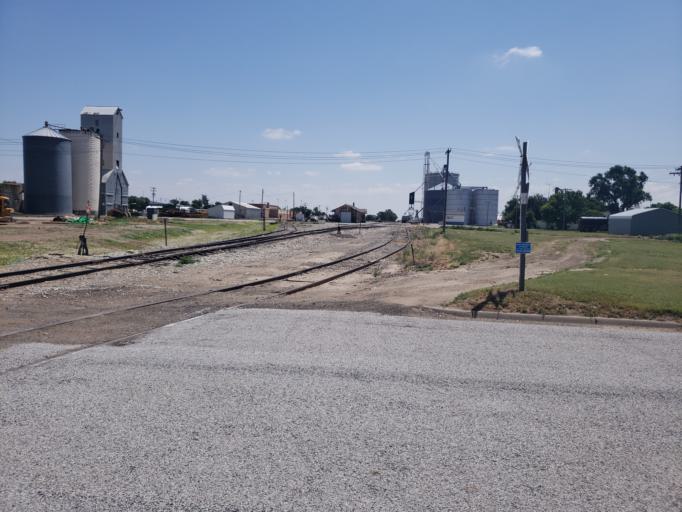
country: US
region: Kansas
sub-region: Ness County
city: Ness City
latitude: 38.4516
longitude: -99.9037
